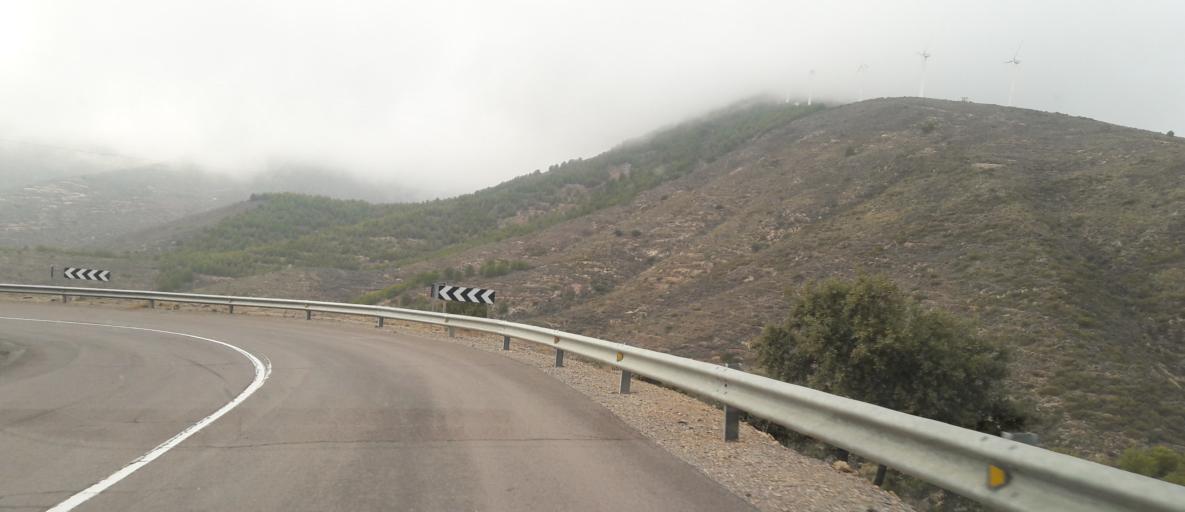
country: ES
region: Andalusia
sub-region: Provincia de Almeria
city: Enix
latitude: 36.8939
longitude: -2.6124
